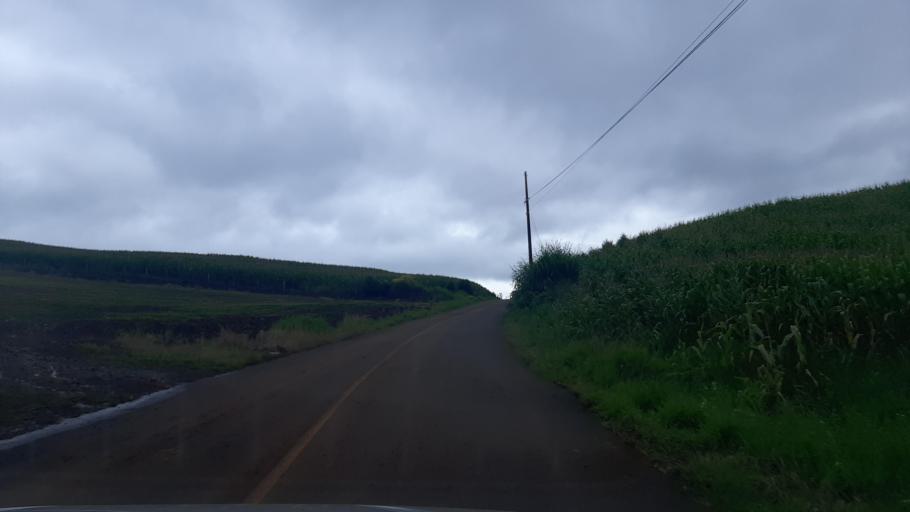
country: BR
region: Parana
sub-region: Ampere
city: Ampere
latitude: -26.0416
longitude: -53.4935
